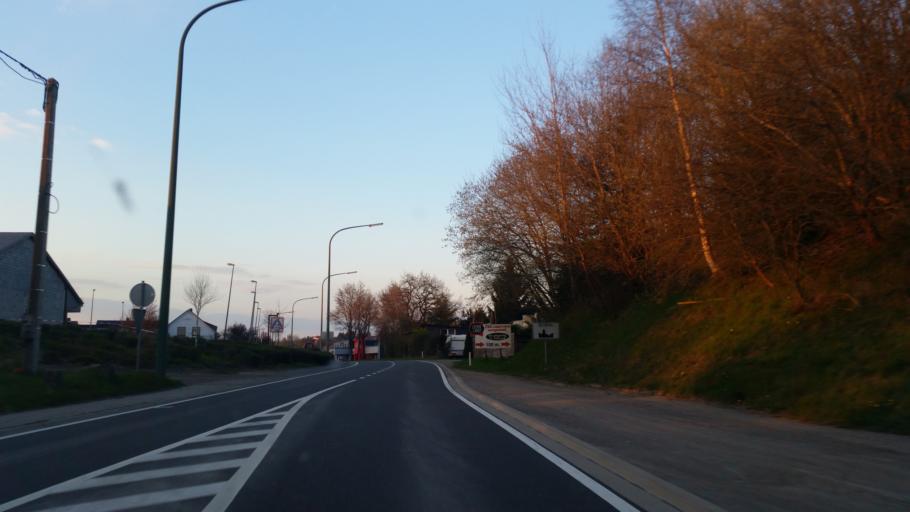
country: BE
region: Wallonia
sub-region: Province de Liege
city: Saint-Vith
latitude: 50.2713
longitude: 6.1174
